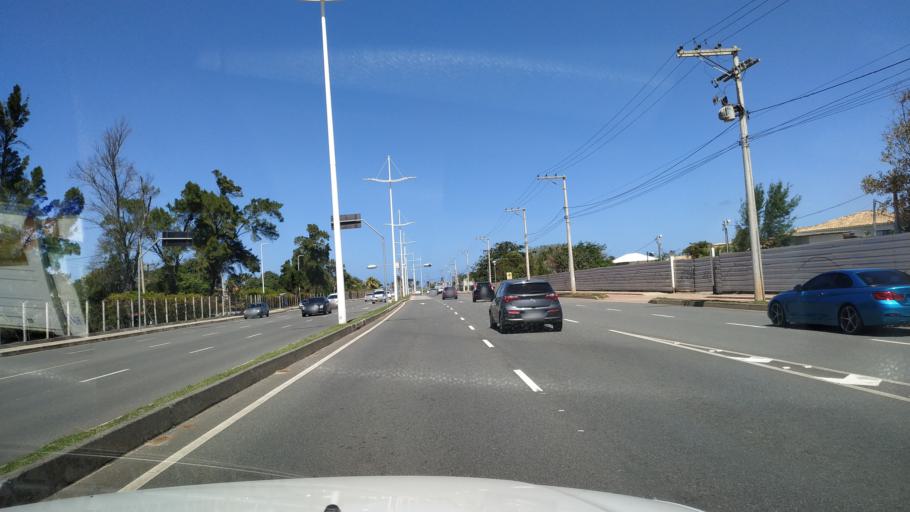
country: BR
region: Bahia
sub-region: Lauro De Freitas
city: Lauro de Freitas
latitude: -12.9503
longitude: -38.3848
